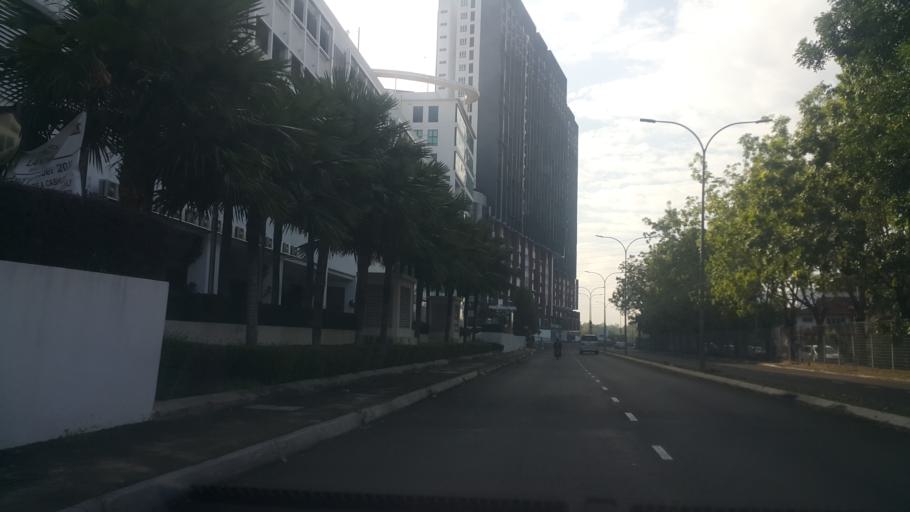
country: MY
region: Selangor
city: Klang
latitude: 2.9950
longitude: 101.4424
